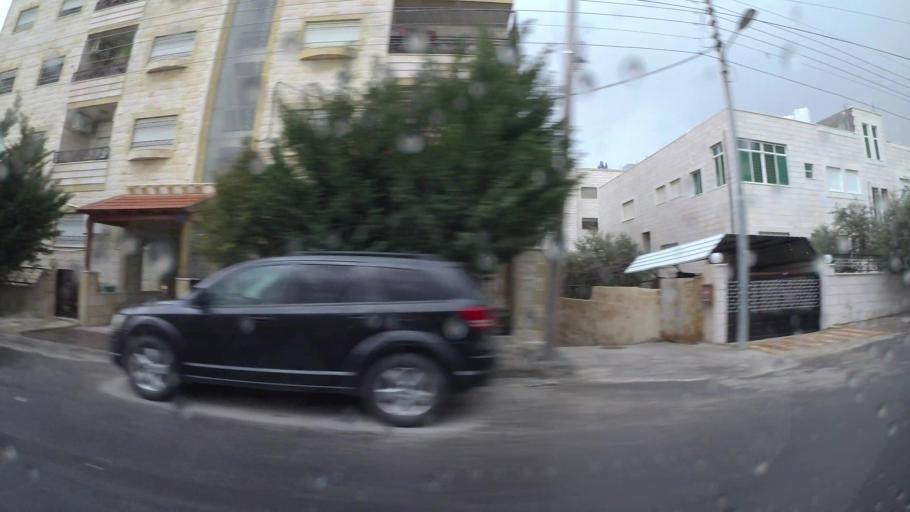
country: JO
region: Amman
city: Amman
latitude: 32.0077
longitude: 35.9562
